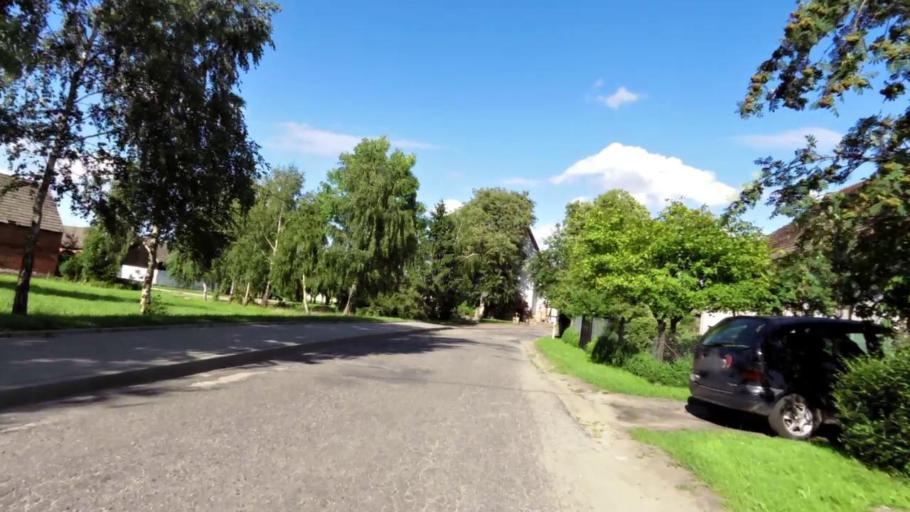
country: PL
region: West Pomeranian Voivodeship
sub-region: Powiat slawienski
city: Slawno
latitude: 54.4351
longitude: 16.7377
